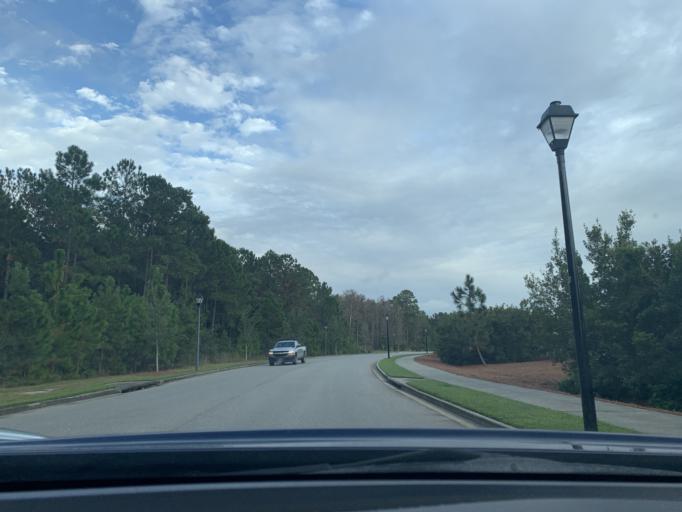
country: US
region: Georgia
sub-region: Chatham County
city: Pooler
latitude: 32.0748
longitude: -81.2604
